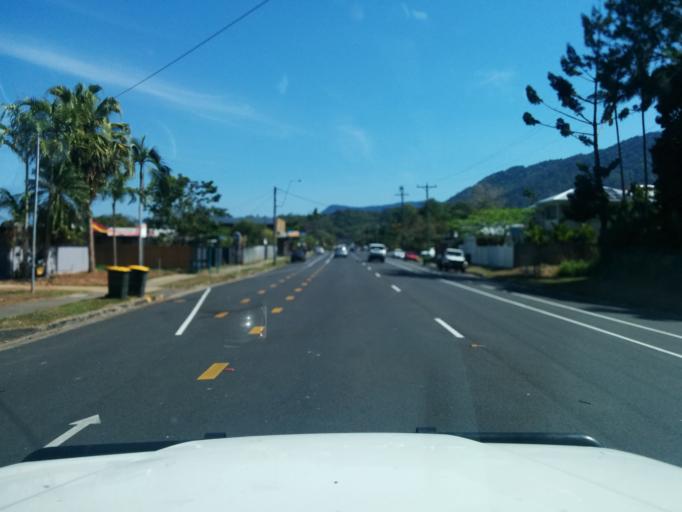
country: AU
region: Queensland
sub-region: Cairns
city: Redlynch
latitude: -16.9033
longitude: 145.7288
